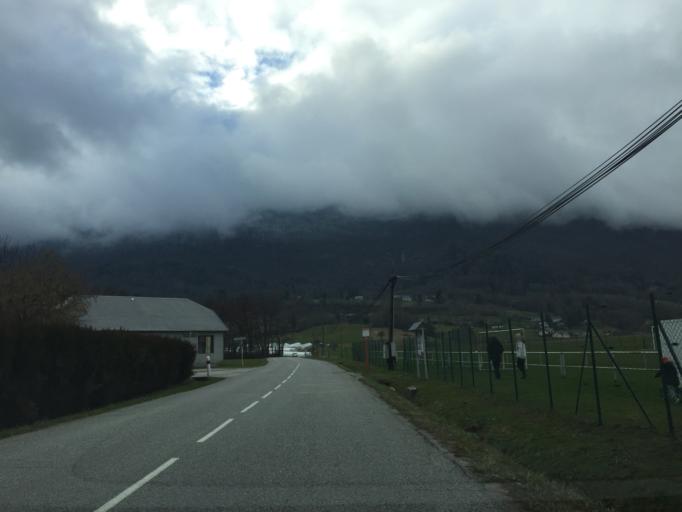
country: FR
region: Rhone-Alpes
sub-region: Departement de la Savoie
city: Vimines
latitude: 45.5382
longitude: 5.8588
